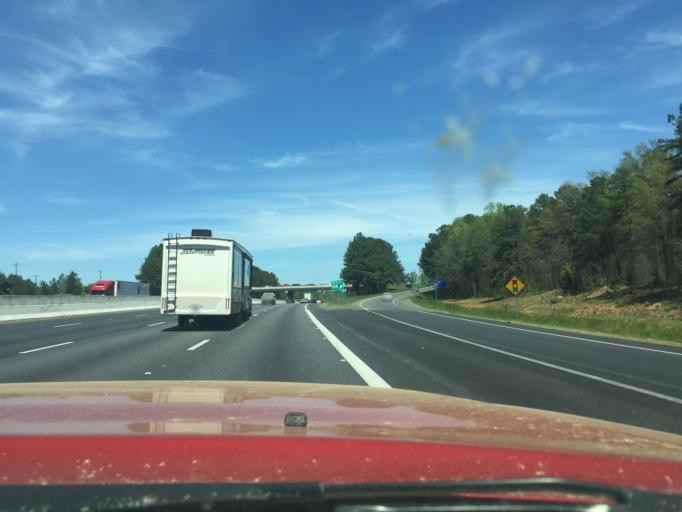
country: US
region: South Carolina
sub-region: York County
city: Fort Mill
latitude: 35.0585
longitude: -80.9571
